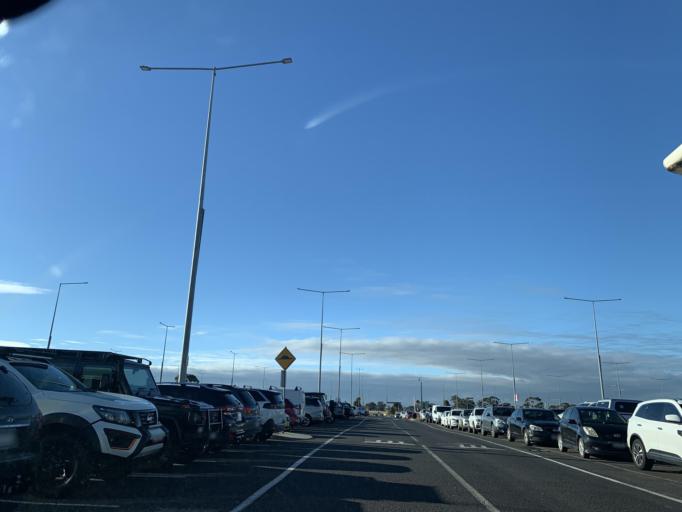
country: AU
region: Victoria
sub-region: Hume
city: Westmeadows
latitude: -37.6789
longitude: 144.8631
